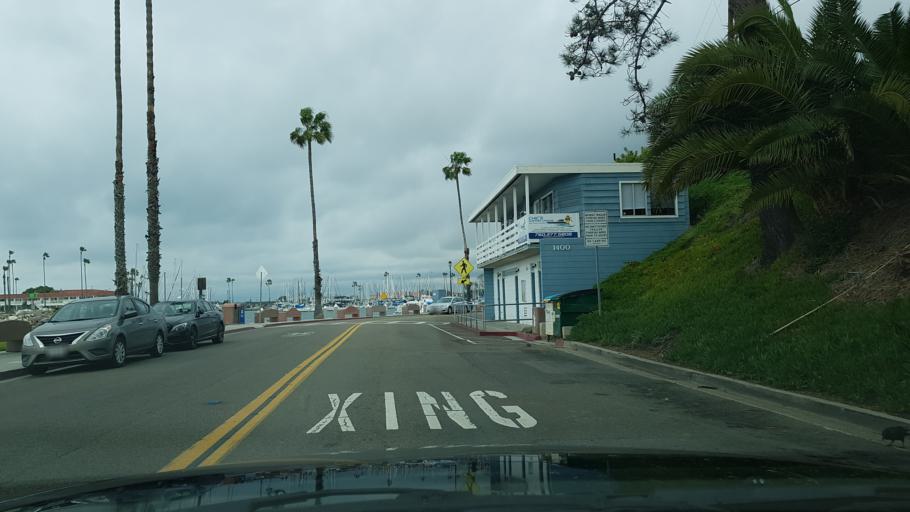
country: US
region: California
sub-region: San Diego County
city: Oceanside
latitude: 33.2081
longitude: -117.3940
